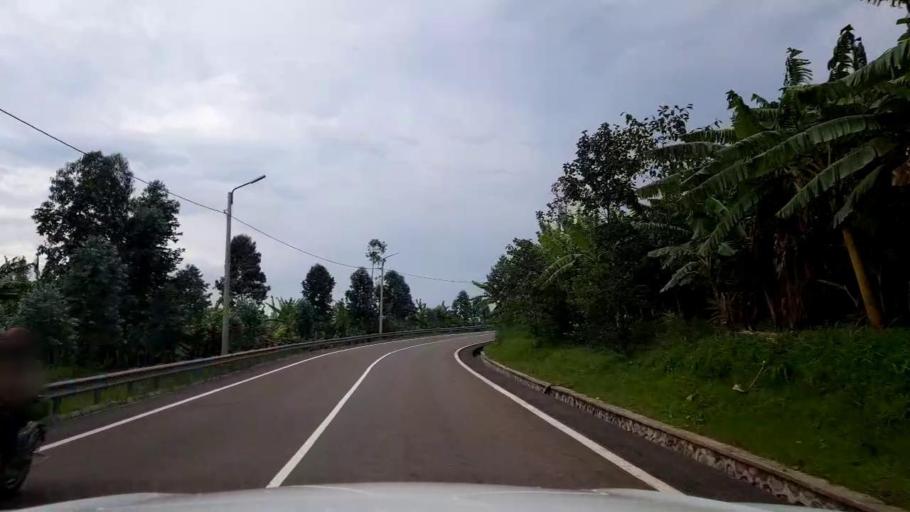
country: RW
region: Western Province
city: Kibuye
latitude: -2.0310
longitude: 29.3956
